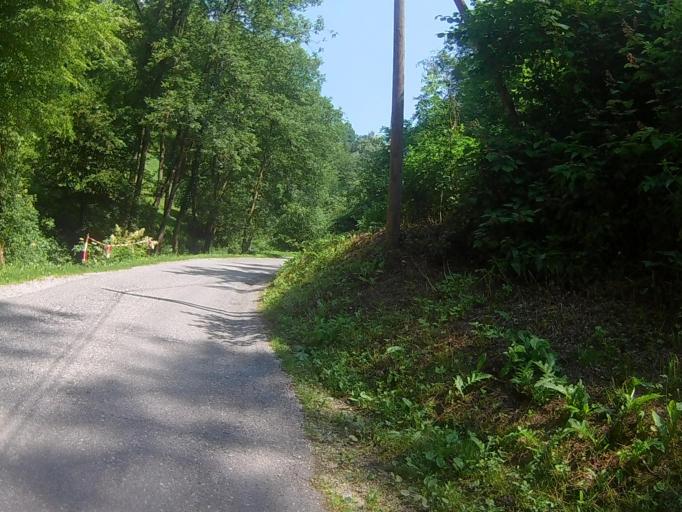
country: SI
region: Maribor
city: Bresternica
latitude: 46.5700
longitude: 15.5750
